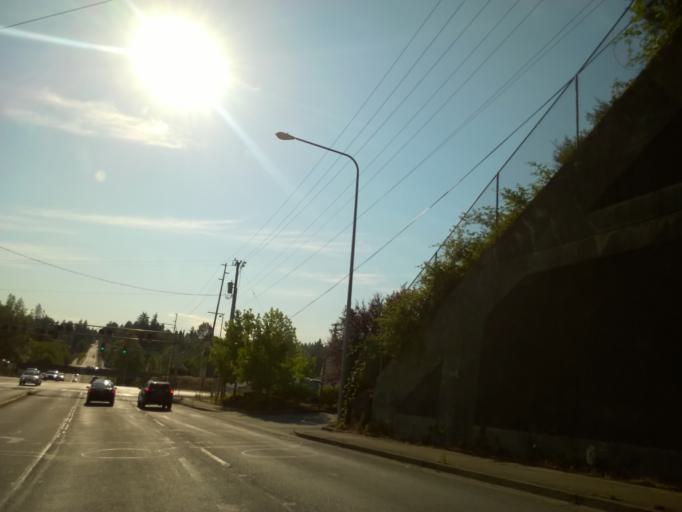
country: US
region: Washington
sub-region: King County
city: Woodinville
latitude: 47.7689
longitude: -122.1547
